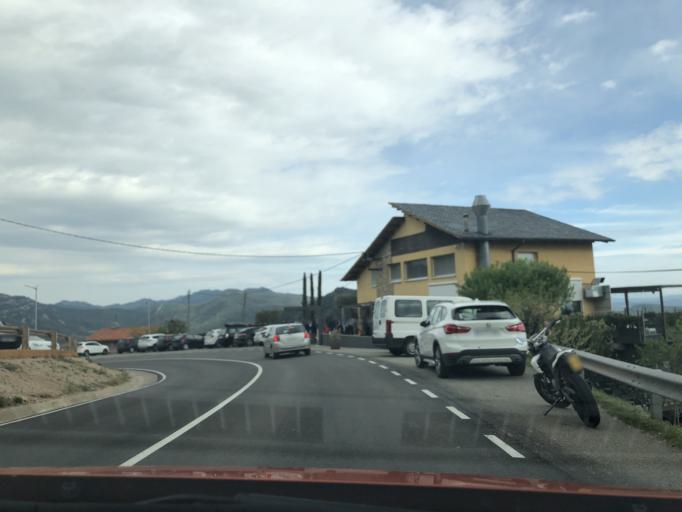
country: ES
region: Catalonia
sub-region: Provincia de Barcelona
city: Berga
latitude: 42.1075
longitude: 1.8512
